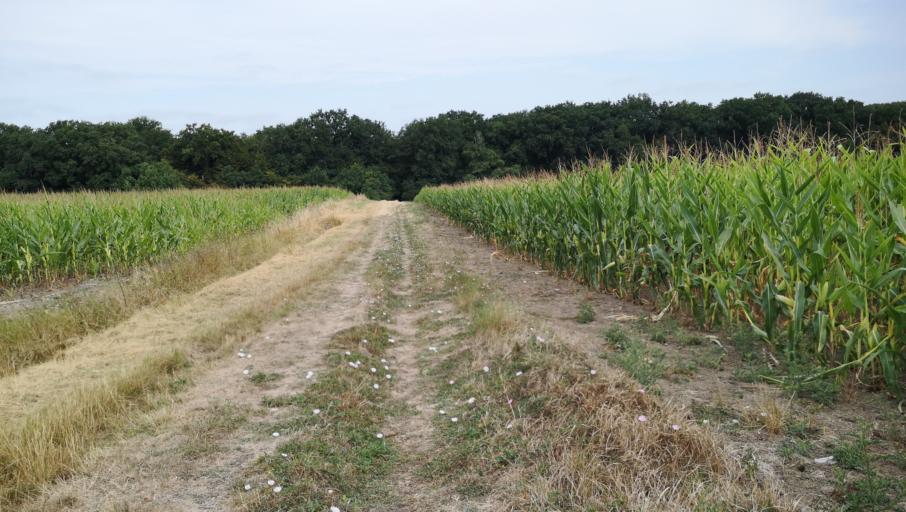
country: FR
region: Centre
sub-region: Departement du Loiret
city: Marigny-les-Usages
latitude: 47.9636
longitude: 2.0122
